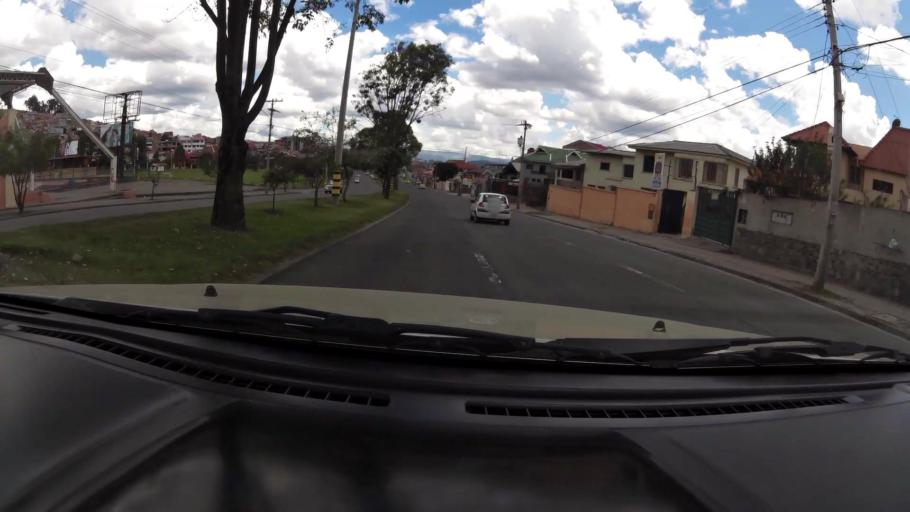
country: EC
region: Azuay
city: Cuenca
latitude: -2.8857
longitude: -78.9934
